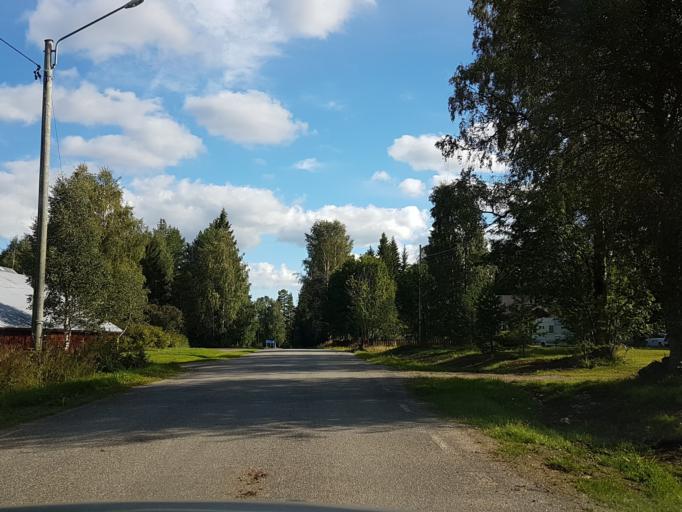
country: SE
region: Vaesterbotten
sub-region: Robertsfors Kommun
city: Robertsfors
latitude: 64.1614
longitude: 20.6512
